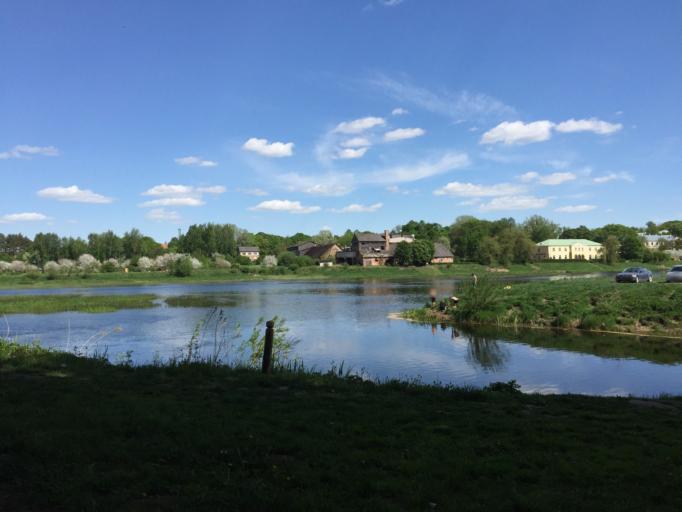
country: LV
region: Rundales
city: Pilsrundale
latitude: 56.4404
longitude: 24.0457
